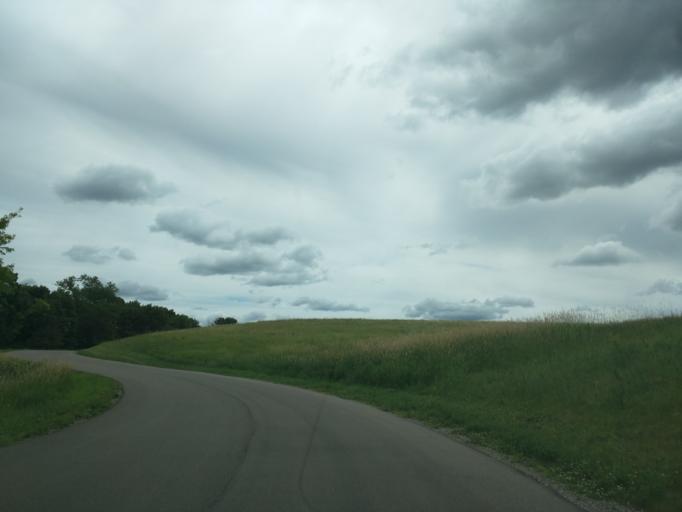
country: US
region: Minnesota
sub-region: Carver County
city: Victoria
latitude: 44.8521
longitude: -93.6103
